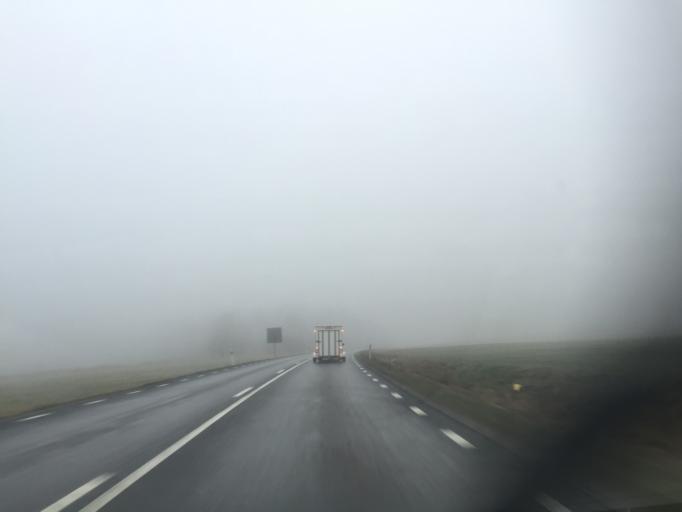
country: SE
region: Soedermanland
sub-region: Katrineholms Kommun
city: Katrineholm
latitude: 58.9522
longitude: 16.3722
